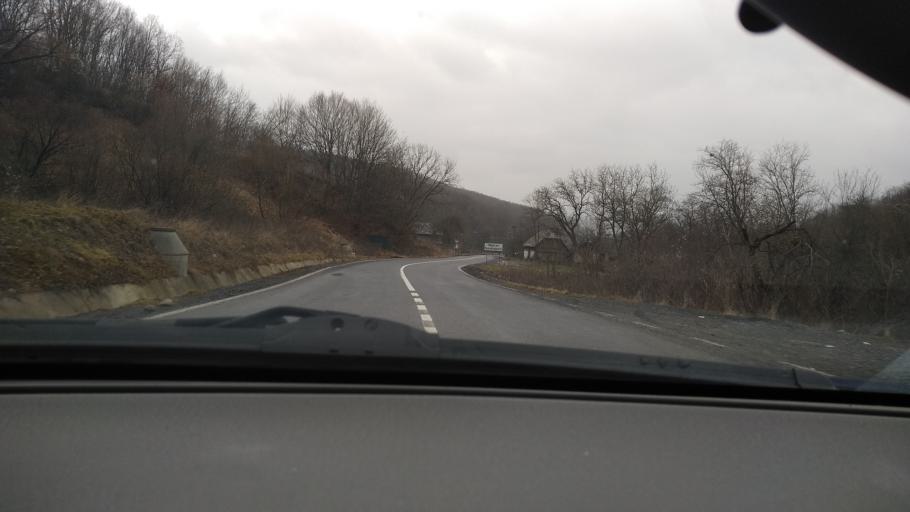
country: RO
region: Mures
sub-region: Comuna Magherani
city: Magherani
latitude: 46.5806
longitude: 24.9361
